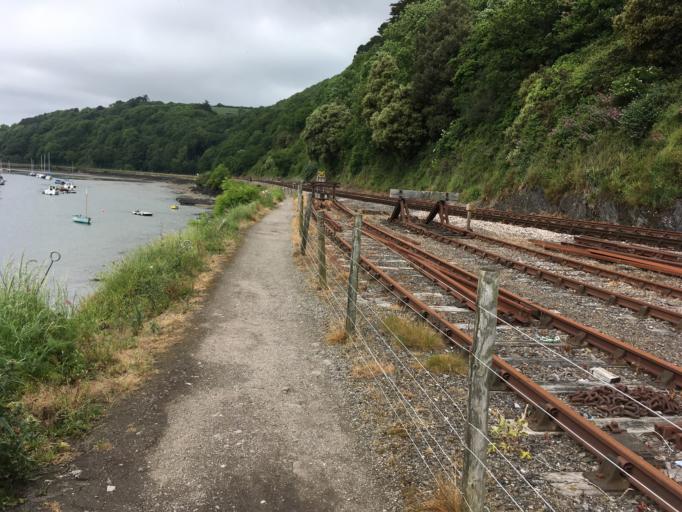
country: GB
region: England
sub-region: Devon
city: Dartmouth
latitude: 50.3527
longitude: -3.5704
